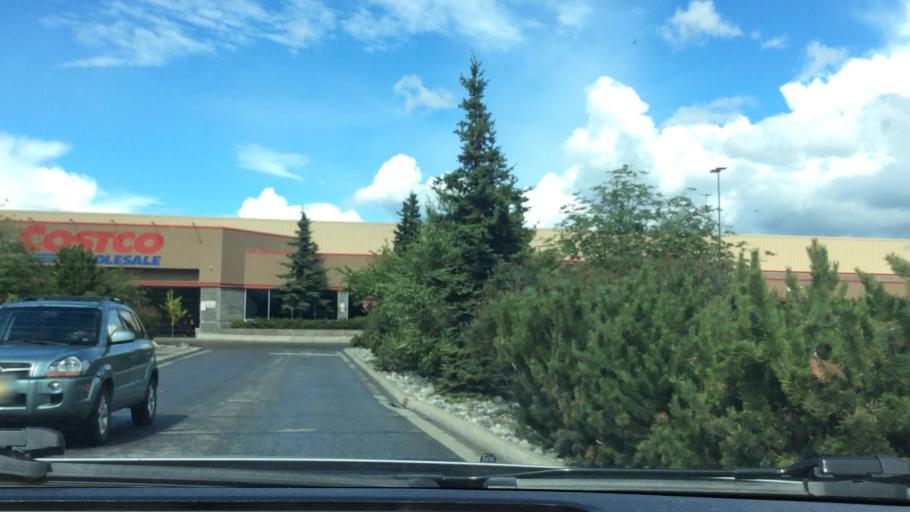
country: US
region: Alaska
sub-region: Anchorage Municipality
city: Anchorage
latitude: 61.2100
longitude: -149.8043
